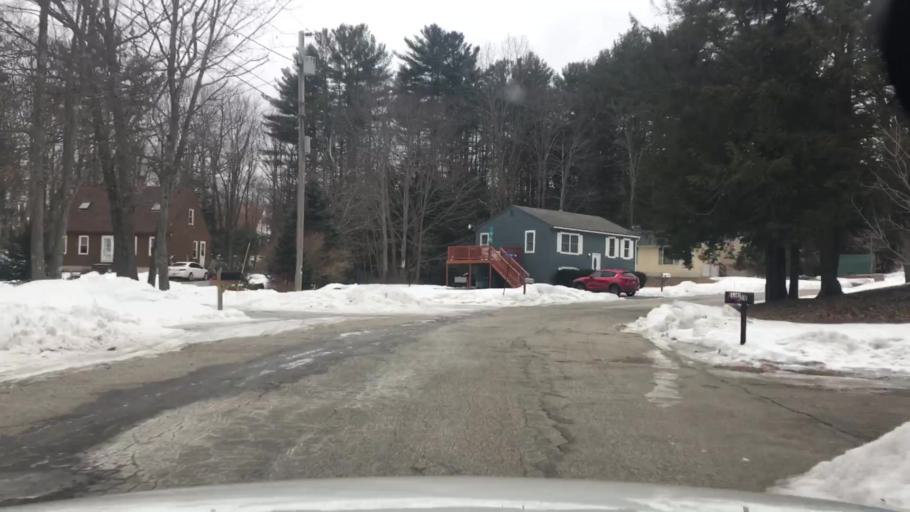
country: US
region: Maine
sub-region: York County
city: Springvale
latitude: 43.4707
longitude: -70.7904
